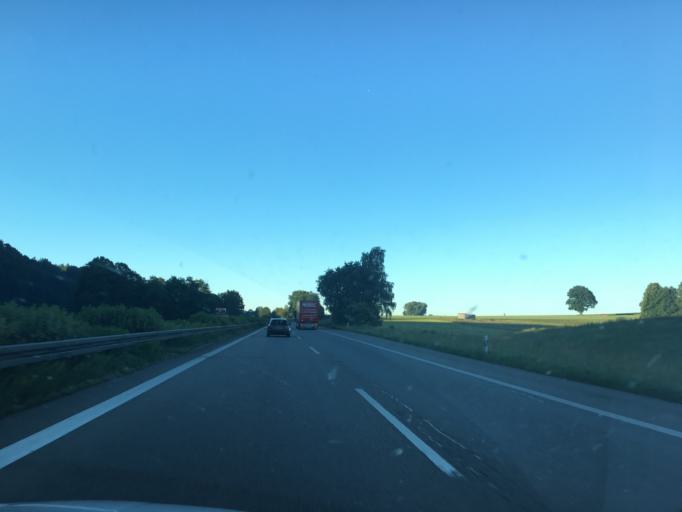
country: DE
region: Bavaria
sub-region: Swabia
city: Altenstadt
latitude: 48.1841
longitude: 10.1265
